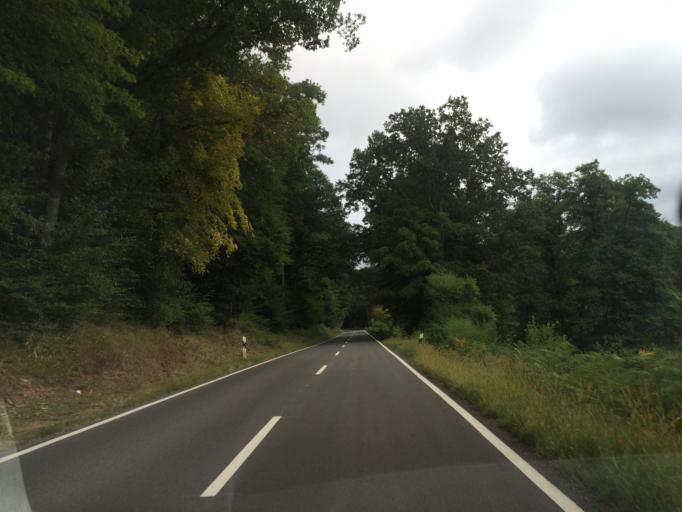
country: DE
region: Rheinland-Pfalz
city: Ruppertsweiler
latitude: 49.1635
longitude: 7.7065
